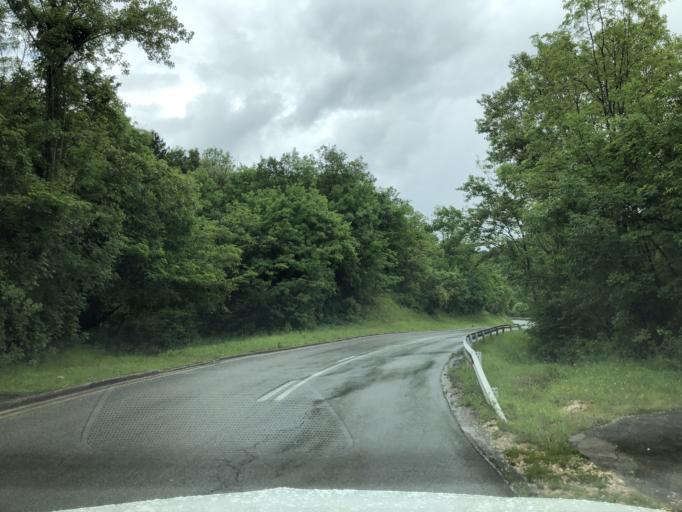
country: SI
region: Koper-Capodistria
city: Prade
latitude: 45.5080
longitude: 13.7758
